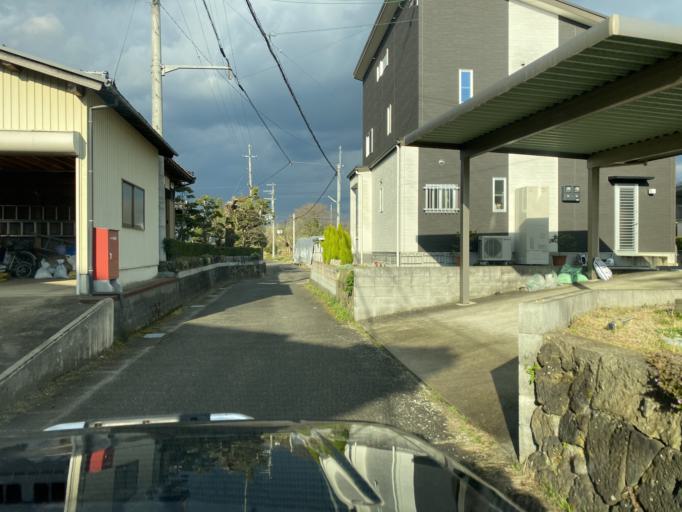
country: JP
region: Hyogo
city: Toyooka
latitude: 35.4941
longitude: 134.8063
